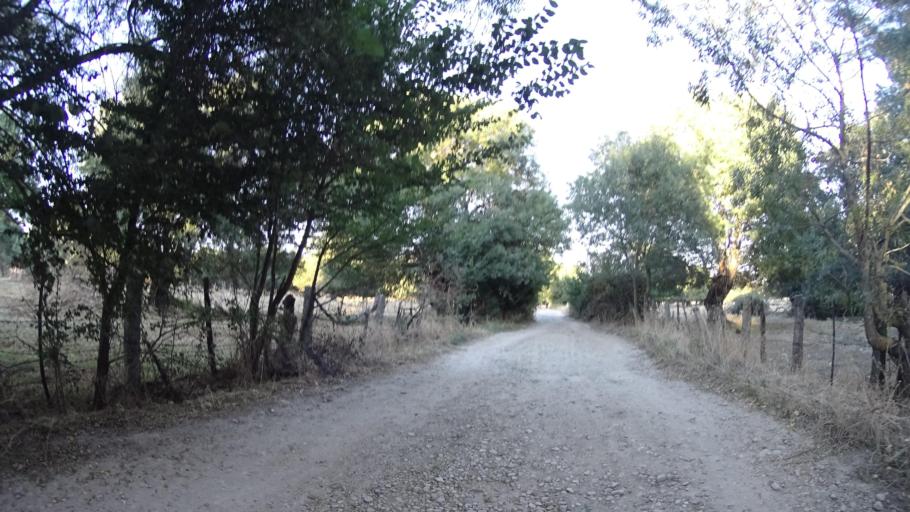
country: ES
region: Madrid
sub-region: Provincia de Madrid
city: Navalquejigo
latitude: 40.6377
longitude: -4.0546
